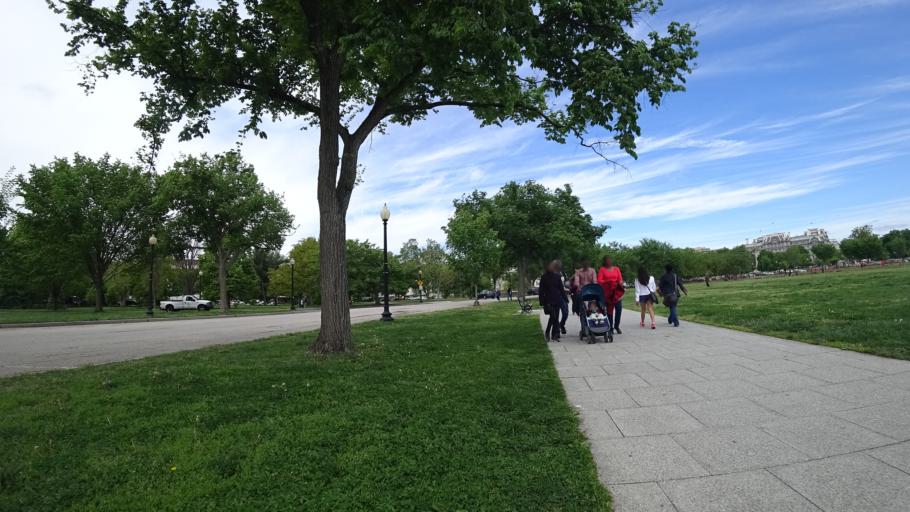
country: US
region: Washington, D.C.
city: Washington, D.C.
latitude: 38.8931
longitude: -77.0378
